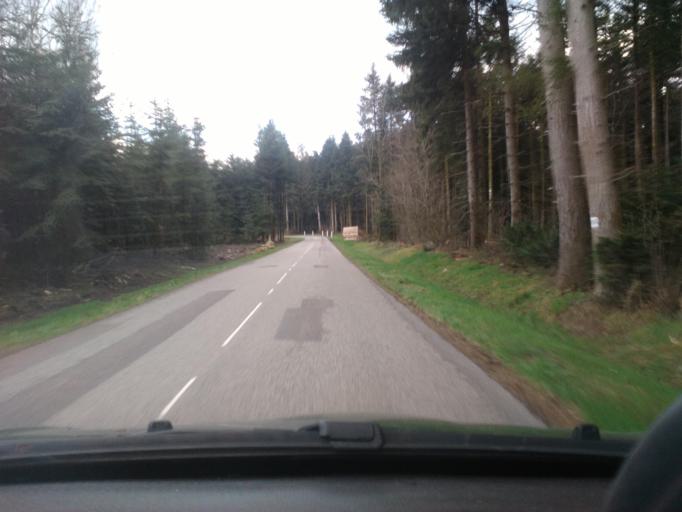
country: FR
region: Lorraine
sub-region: Departement des Vosges
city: Etival-Clairefontaine
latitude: 48.3340
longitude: 6.8232
